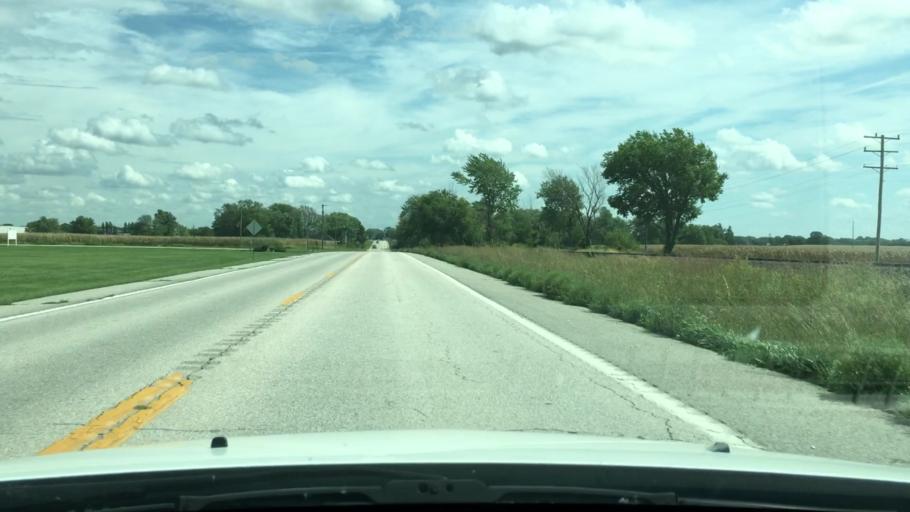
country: US
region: Missouri
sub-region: Audrain County
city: Vandalia
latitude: 39.2986
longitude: -91.5138
